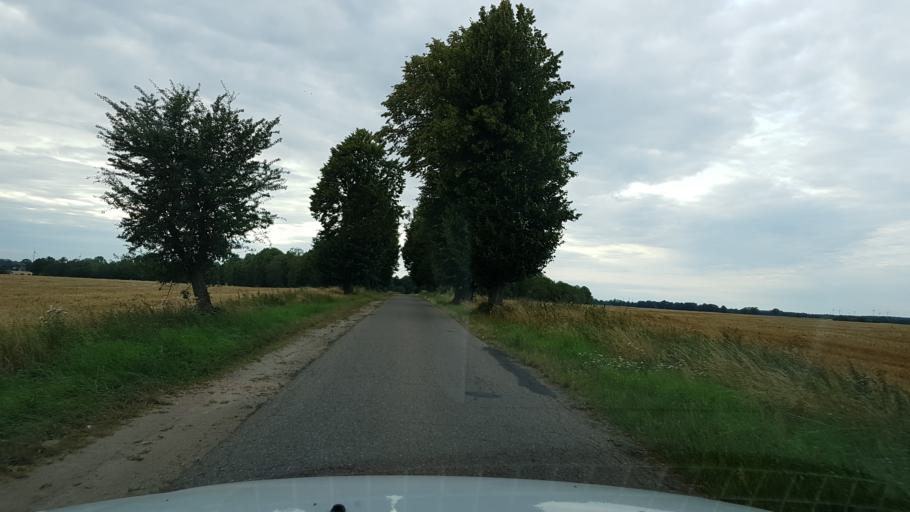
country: PL
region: West Pomeranian Voivodeship
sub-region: Powiat bialogardzki
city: Karlino
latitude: 54.1145
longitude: 15.8757
